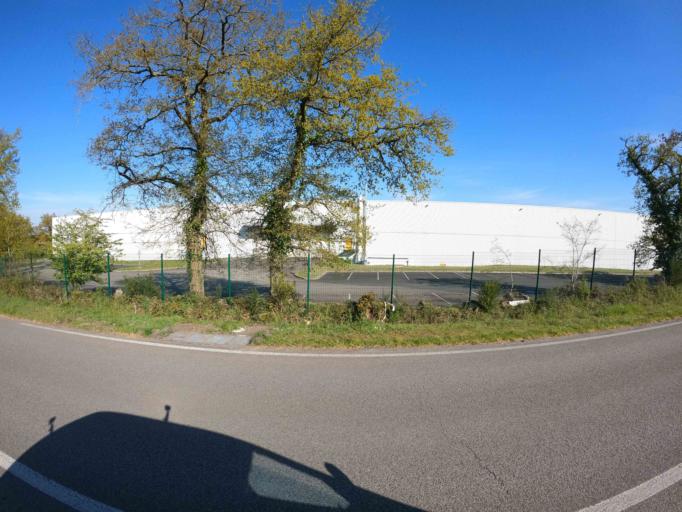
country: FR
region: Pays de la Loire
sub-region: Departement de la Vendee
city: Mortagne-sur-Sevre
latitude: 46.9790
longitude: -0.9650
